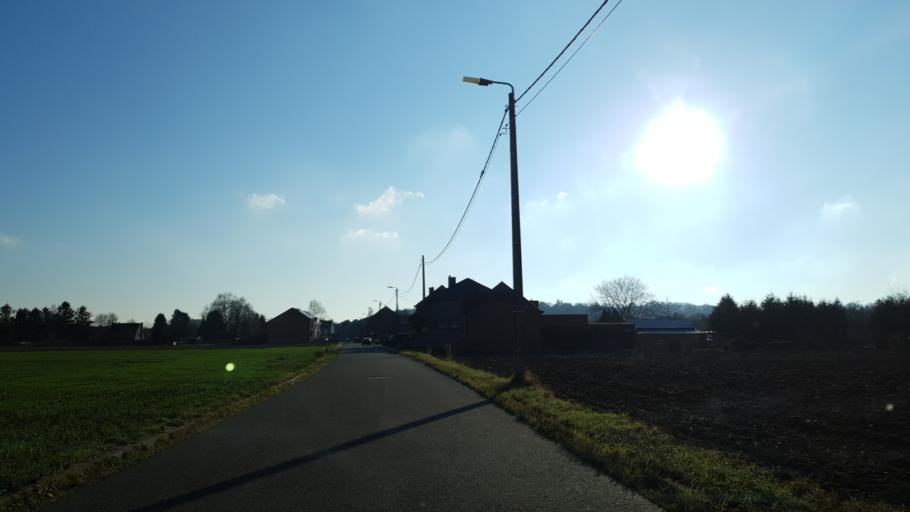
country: BE
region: Flanders
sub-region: Provincie Vlaams-Brabant
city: Herent
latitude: 50.9085
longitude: 4.6939
